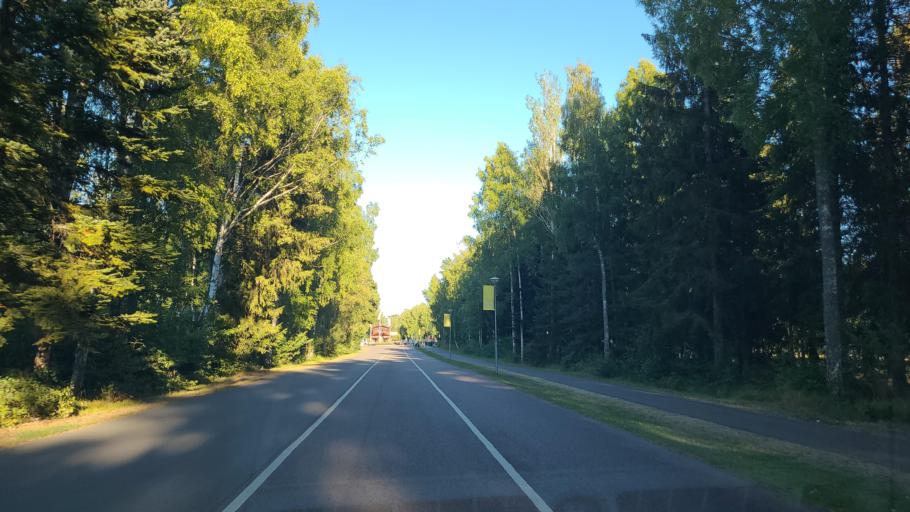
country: SE
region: Kalmar
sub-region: Borgholms Kommun
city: Borgholm
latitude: 57.2751
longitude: 17.0450
